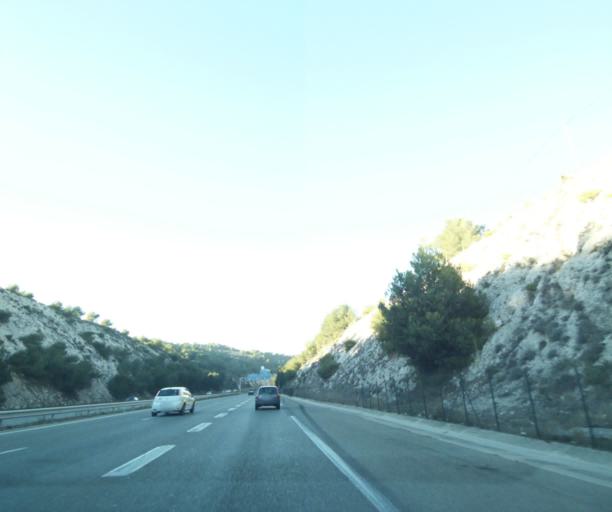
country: FR
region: Provence-Alpes-Cote d'Azur
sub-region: Departement des Bouches-du-Rhone
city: Les Pennes-Mirabeau
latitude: 43.3899
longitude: 5.3032
